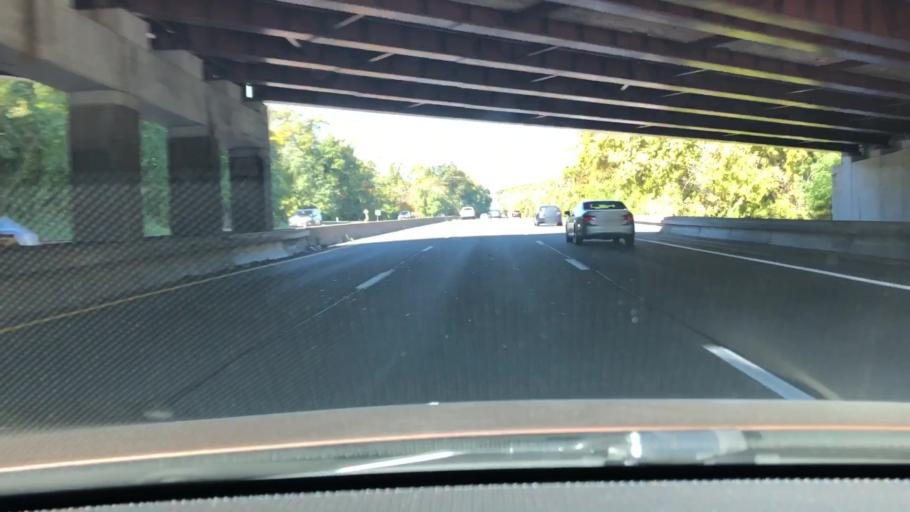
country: US
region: New York
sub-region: Westchester County
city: Bronxville
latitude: 40.9466
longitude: -73.8496
